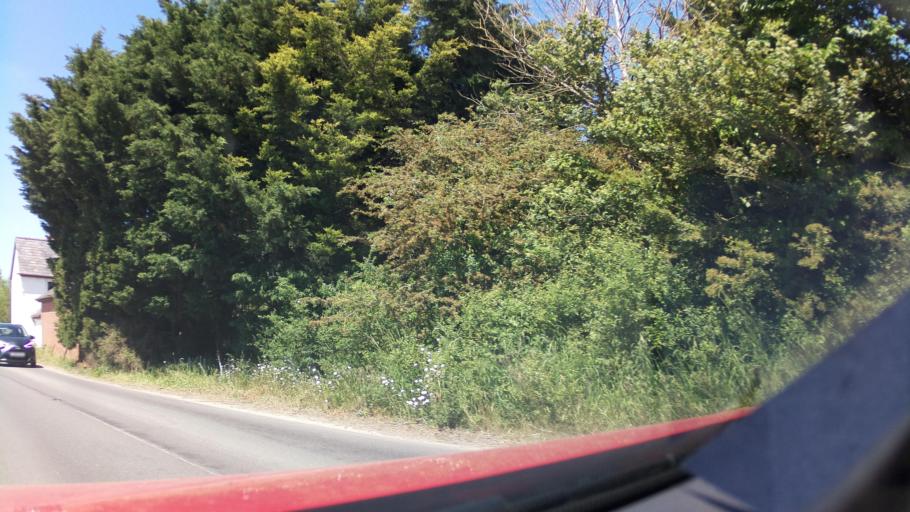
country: GB
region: England
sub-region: Wiltshire
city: Royal Wootton Bassett
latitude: 51.5264
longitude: -1.8921
